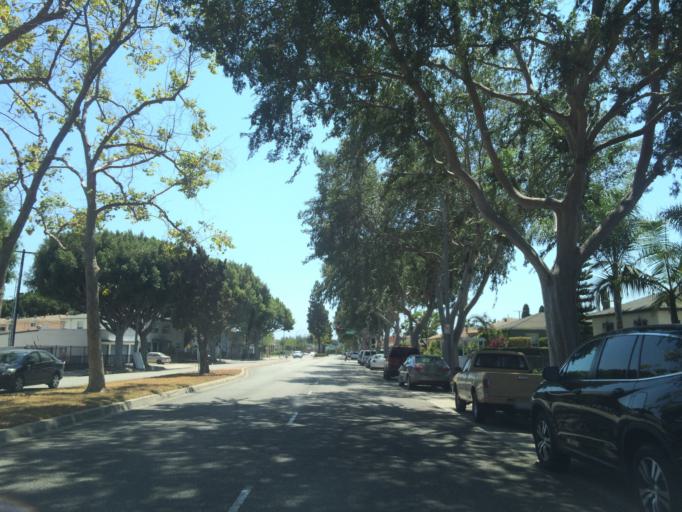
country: US
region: California
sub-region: Los Angeles County
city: Culver City
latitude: 34.0030
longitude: -118.3941
